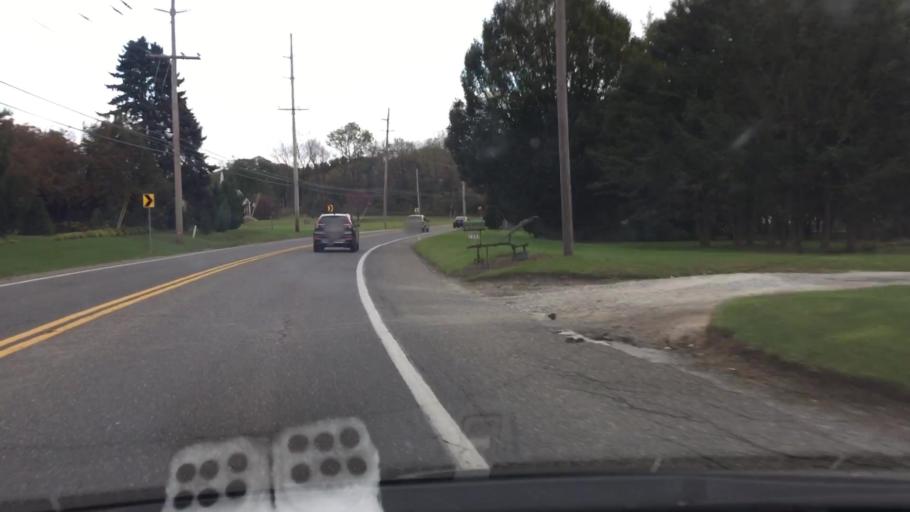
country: US
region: Pennsylvania
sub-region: Delaware County
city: Lima
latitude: 39.9447
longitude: -75.4777
